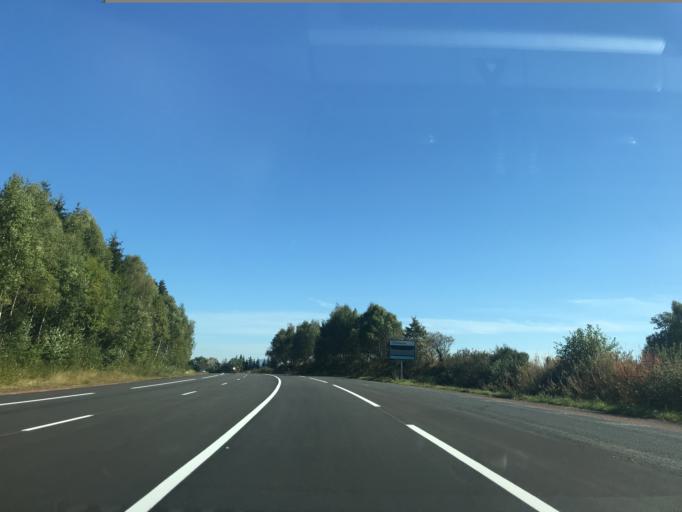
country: FR
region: Auvergne
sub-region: Departement du Puy-de-Dome
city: Saint-Sauves-d'Auvergne
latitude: 45.6550
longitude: 2.6995
